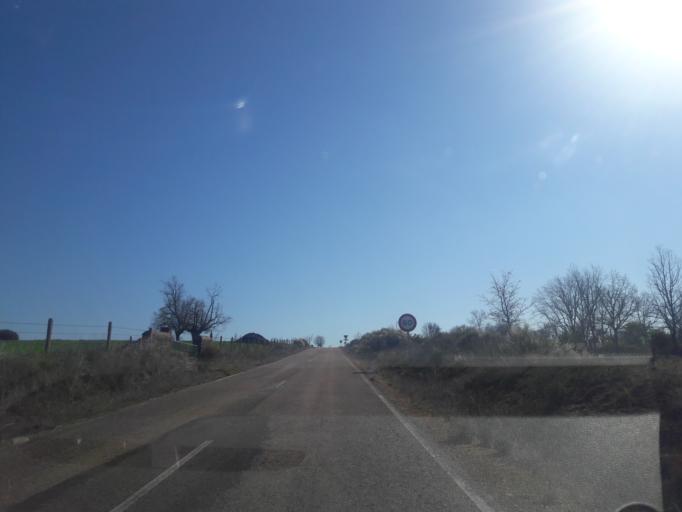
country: ES
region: Castille and Leon
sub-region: Provincia de Salamanca
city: Cabeza del Caballo
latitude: 41.1680
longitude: -6.5337
